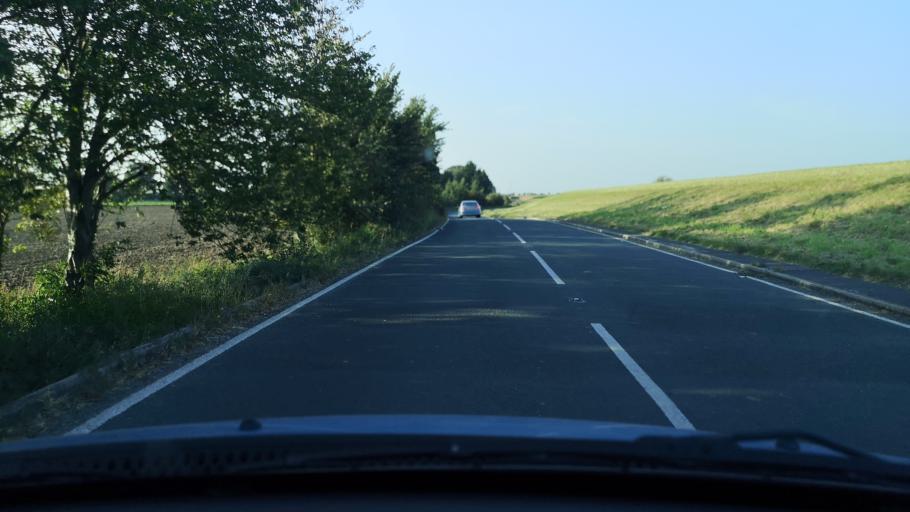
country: GB
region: England
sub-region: East Riding of Yorkshire
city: Goole
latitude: 53.6861
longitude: -0.8602
